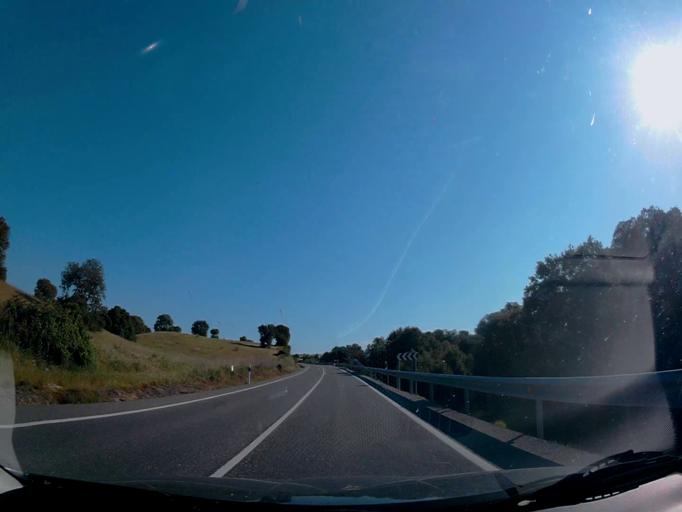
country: ES
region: Castille-La Mancha
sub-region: Province of Toledo
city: Escalona
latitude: 40.1969
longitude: -4.3998
